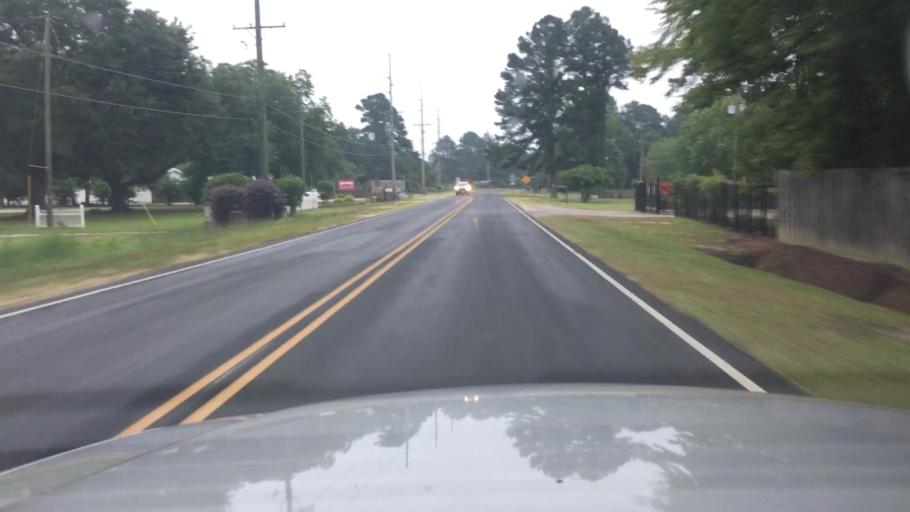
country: US
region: North Carolina
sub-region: Cumberland County
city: Fayetteville
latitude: 34.9997
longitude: -78.8572
